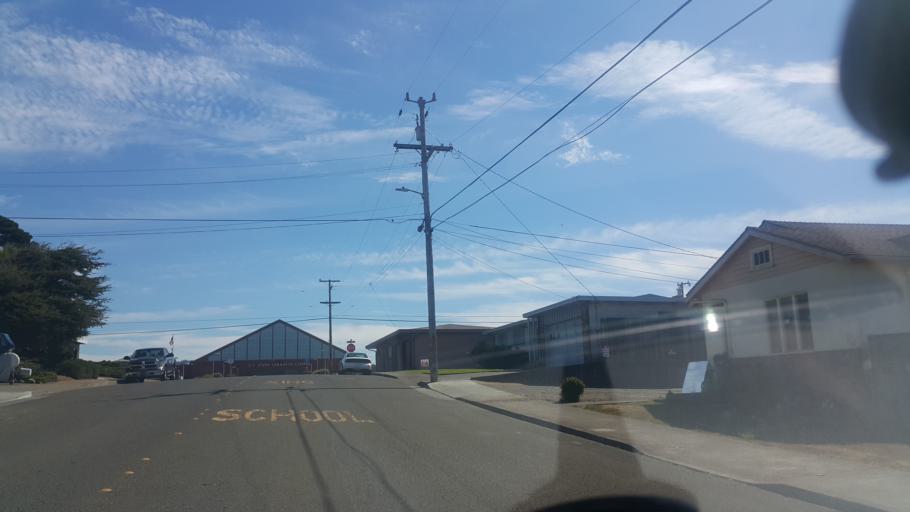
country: US
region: California
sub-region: Mendocino County
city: Fort Bragg
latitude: 39.4391
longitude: -123.7965
